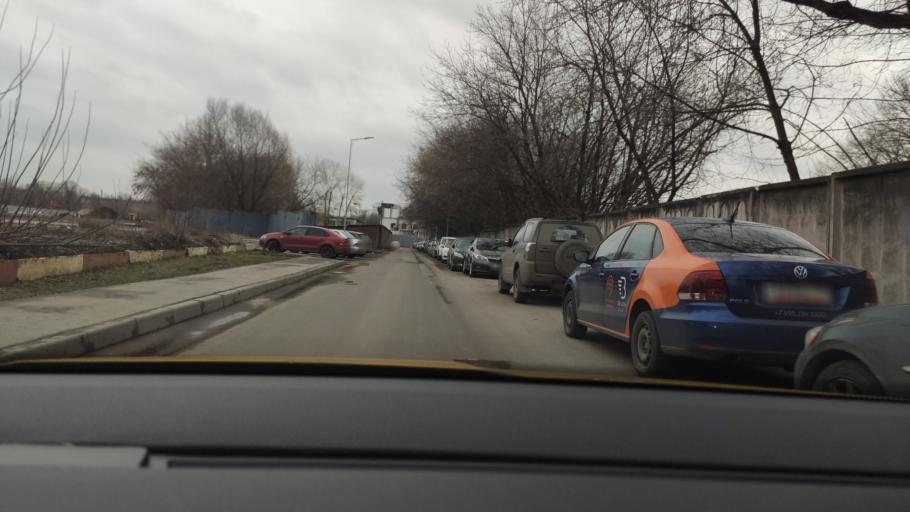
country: RU
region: Moscow
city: Lefortovo
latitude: 55.7294
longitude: 37.7129
